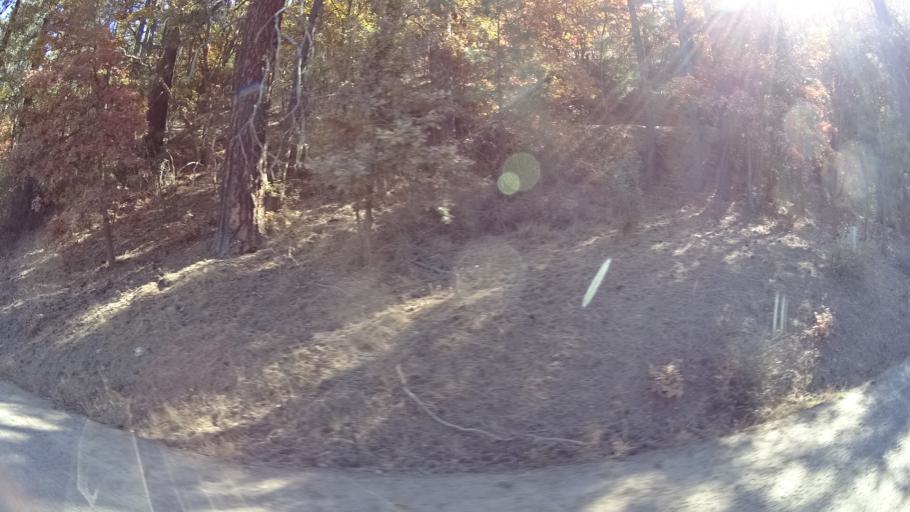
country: US
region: California
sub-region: Siskiyou County
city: Yreka
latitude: 41.5947
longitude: -122.9598
